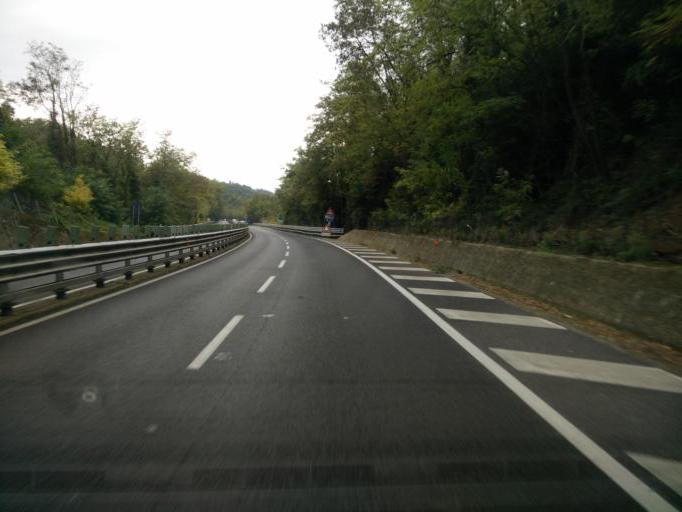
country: IT
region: Tuscany
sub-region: Province of Florence
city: Sambuca
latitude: 43.5665
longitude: 11.2127
